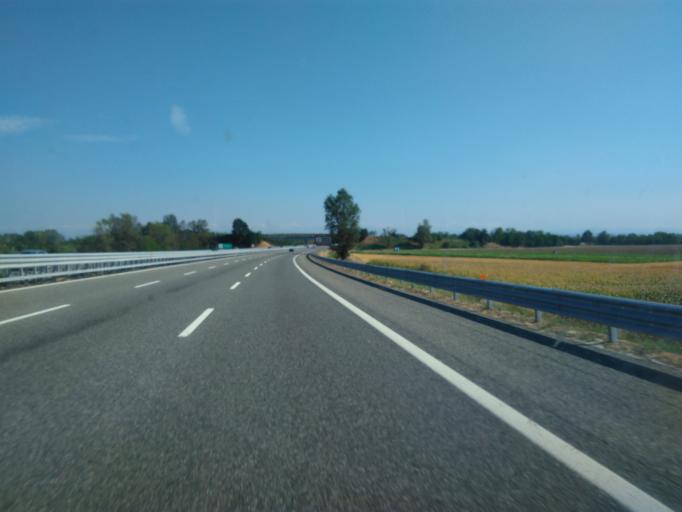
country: IT
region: Piedmont
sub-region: Provincia di Alessandria
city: Castellazzo Bormida
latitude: 44.8472
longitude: 8.5941
